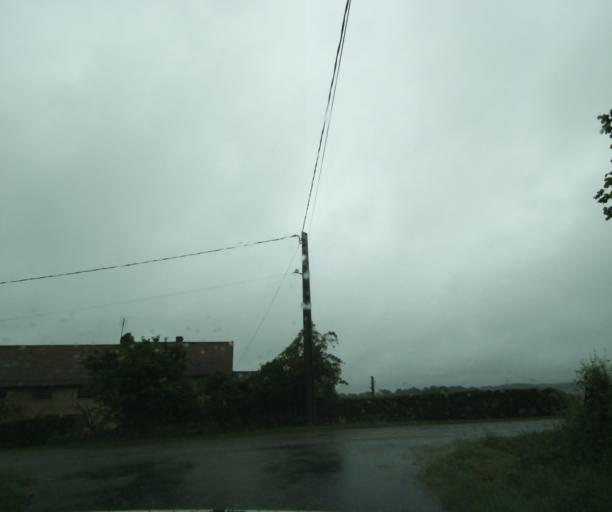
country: FR
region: Bourgogne
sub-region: Departement de Saone-et-Loire
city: Charolles
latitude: 46.4121
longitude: 4.3243
